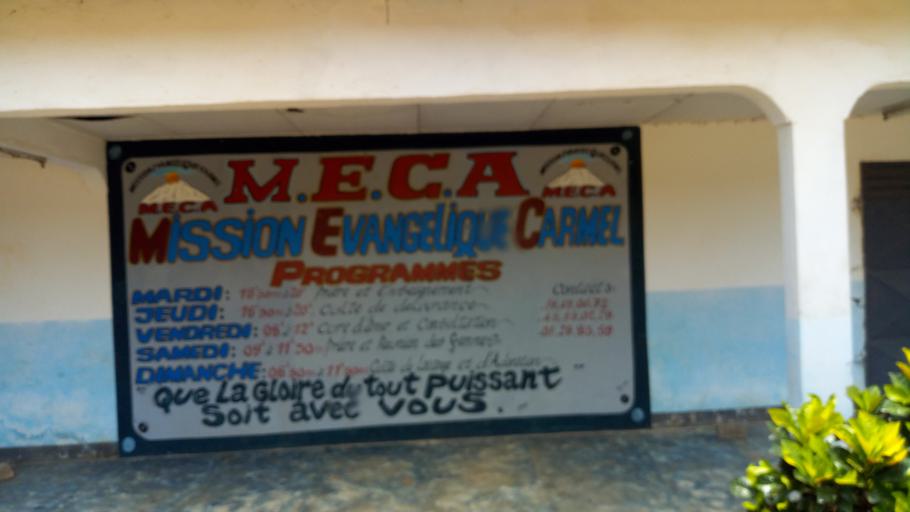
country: CI
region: Vallee du Bandama
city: Bouake
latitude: 7.6681
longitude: -5.0453
